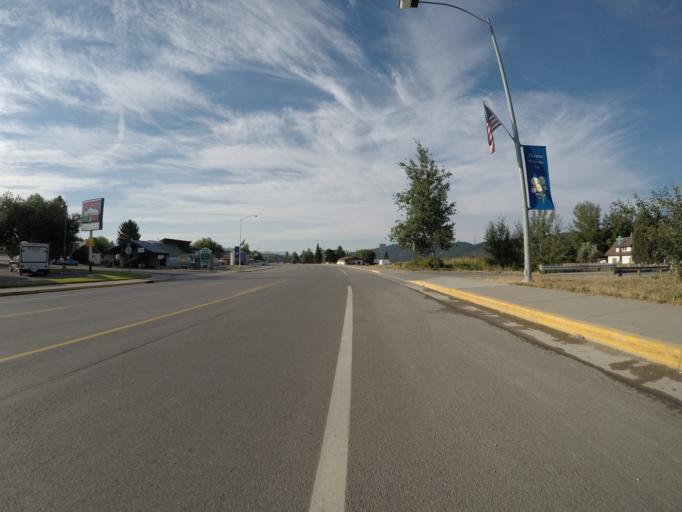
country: US
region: Wyoming
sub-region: Lincoln County
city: Afton
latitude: 42.9176
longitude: -111.0025
